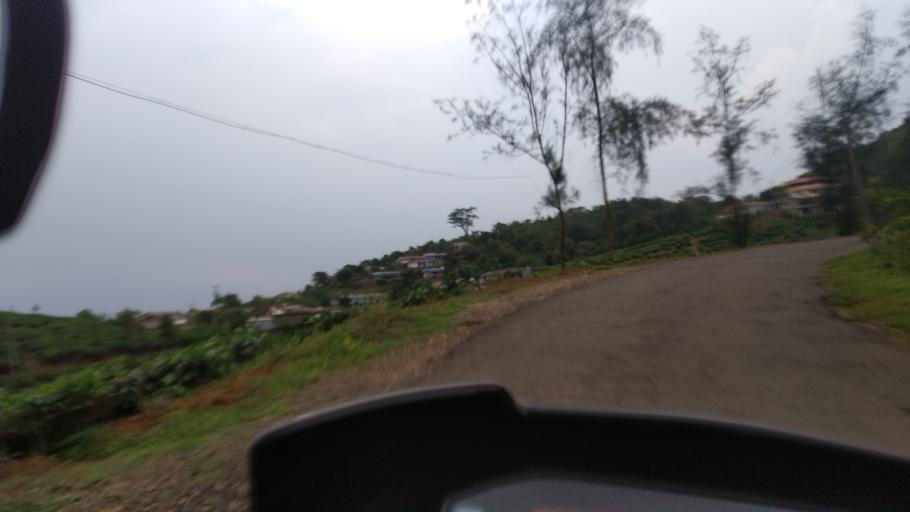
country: IN
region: Tamil Nadu
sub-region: Theni
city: Gudalur
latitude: 9.5450
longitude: 77.0375
